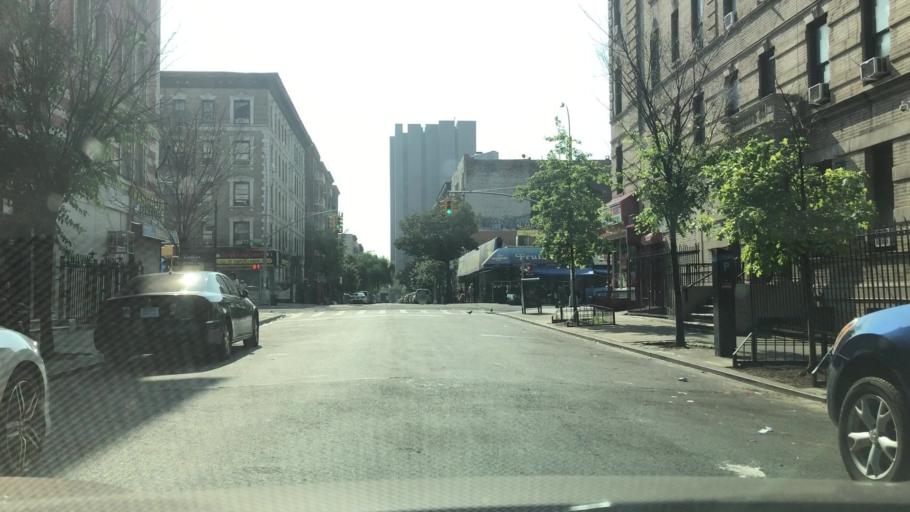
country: US
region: New York
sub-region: New York County
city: Inwood
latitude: 40.8513
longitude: -73.9330
